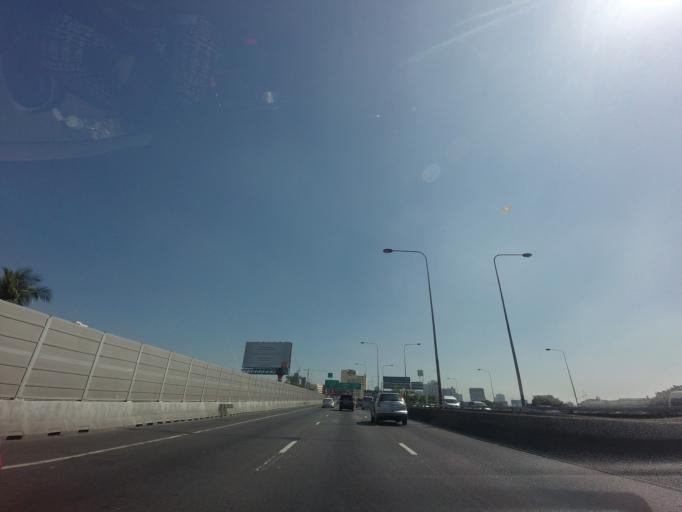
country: TH
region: Bangkok
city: Khlong Toei
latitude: 13.7129
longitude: 100.5716
